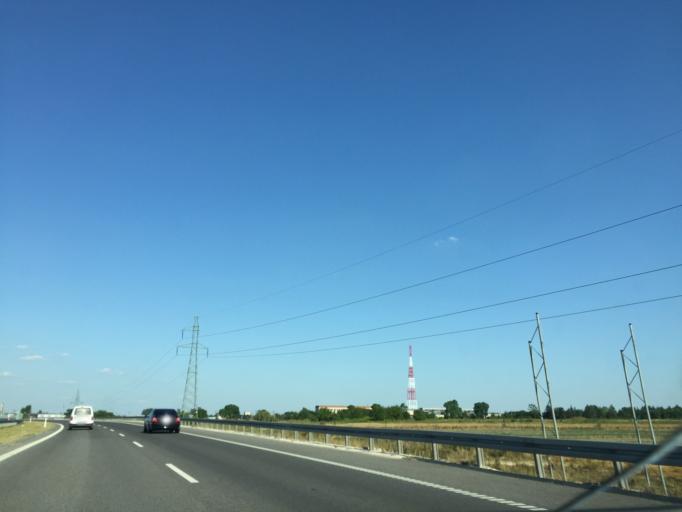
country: PL
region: Swietokrzyskie
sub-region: Powiat jedrzejowski
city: Jedrzejow
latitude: 50.6254
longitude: 20.3044
